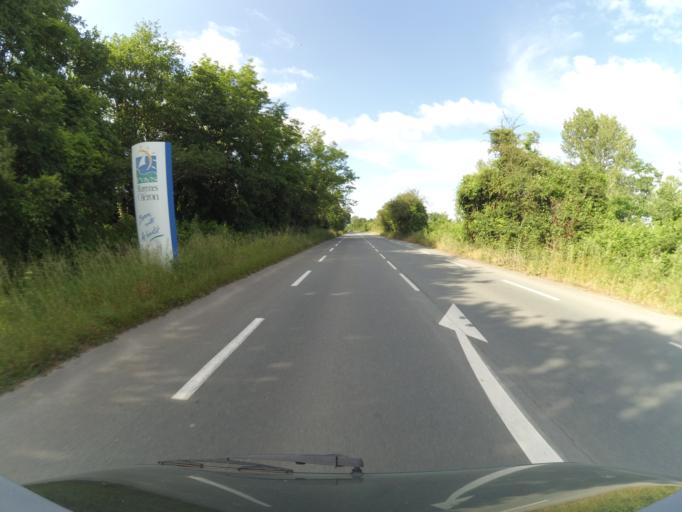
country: FR
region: Poitou-Charentes
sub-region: Departement de la Charente-Maritime
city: Le Gua
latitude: 45.7672
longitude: -0.9388
